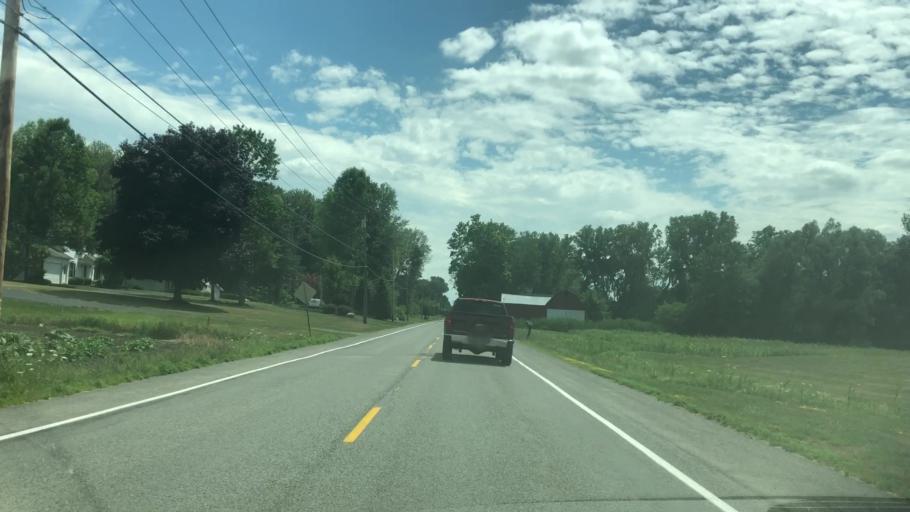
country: US
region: New York
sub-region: Monroe County
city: Fairport
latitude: 43.1465
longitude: -77.4006
